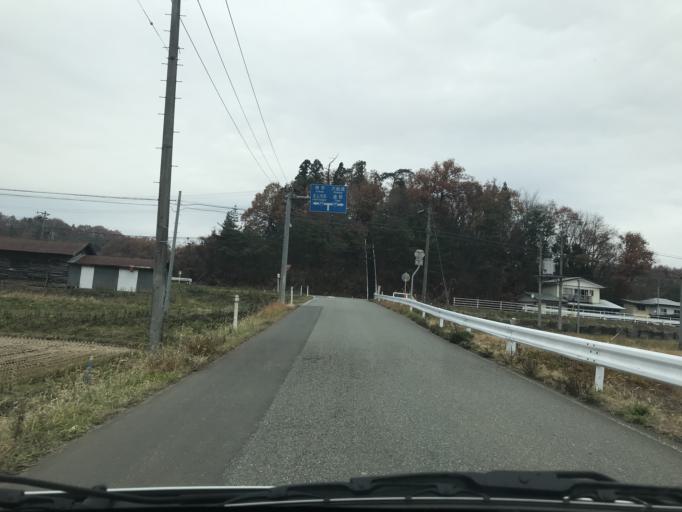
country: JP
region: Iwate
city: Kitakami
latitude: 39.2926
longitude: 141.1743
